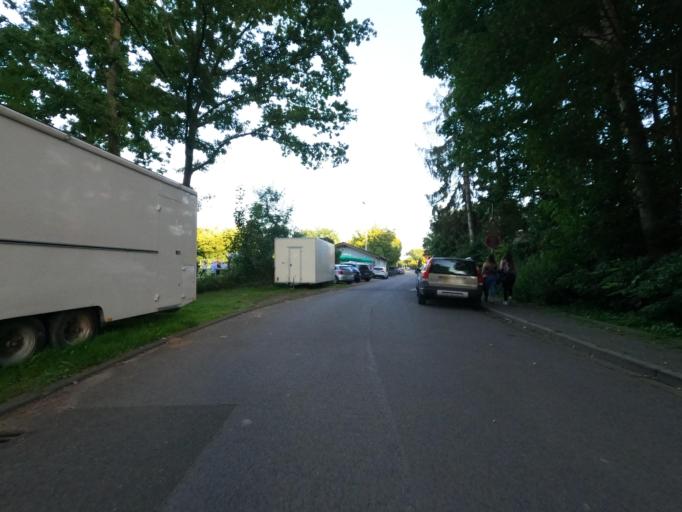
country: DE
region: North Rhine-Westphalia
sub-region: Regierungsbezirk Koln
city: Linnich
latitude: 50.9463
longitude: 6.3097
